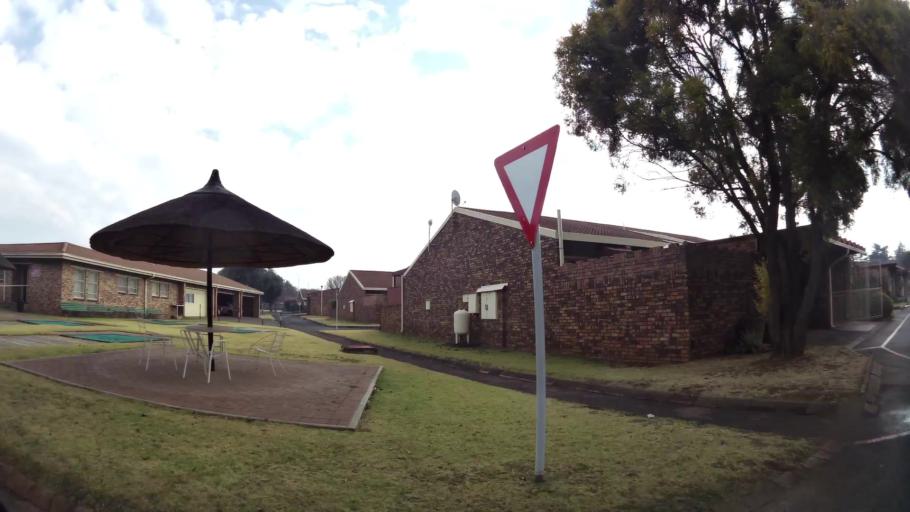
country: ZA
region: Gauteng
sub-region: Sedibeng District Municipality
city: Vanderbijlpark
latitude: -26.7052
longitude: 27.8306
